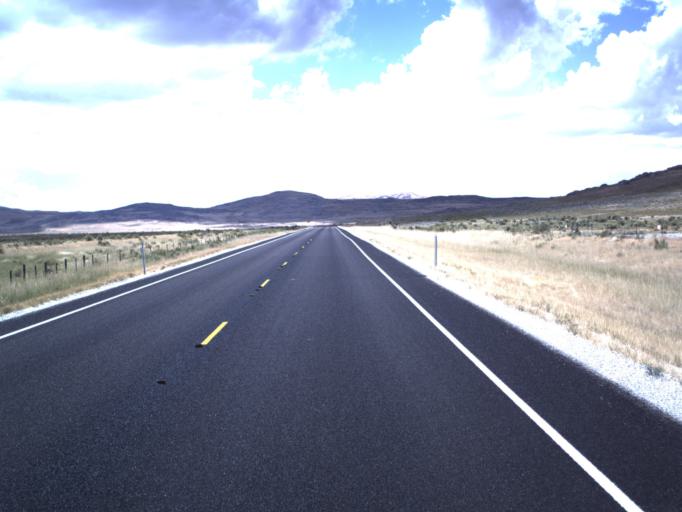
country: US
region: Utah
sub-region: Box Elder County
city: Tremonton
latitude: 41.6288
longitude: -112.4097
